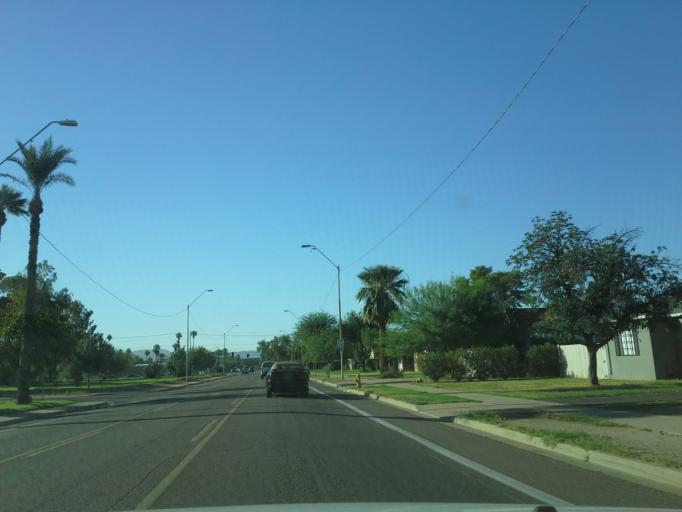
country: US
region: Arizona
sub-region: Maricopa County
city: Phoenix
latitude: 33.4682
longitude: -112.0914
